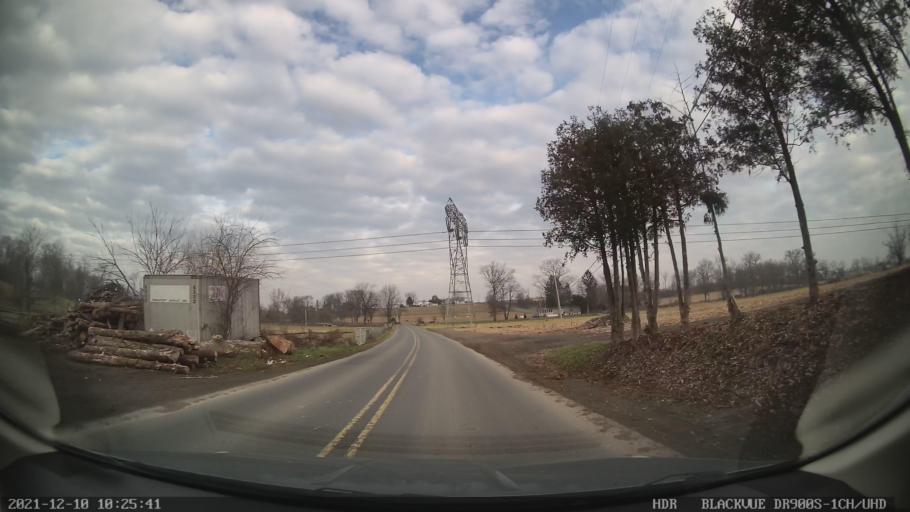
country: US
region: Pennsylvania
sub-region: Berks County
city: Topton
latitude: 40.4908
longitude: -75.7425
